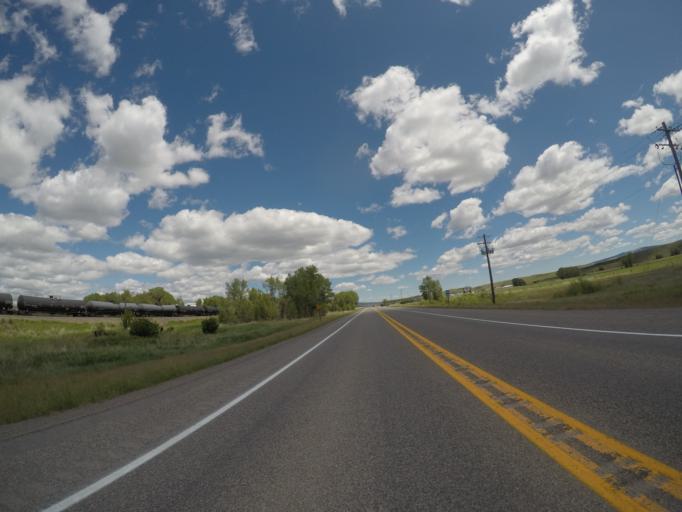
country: US
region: Montana
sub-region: Park County
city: Livingston
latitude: 45.6777
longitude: -110.5297
